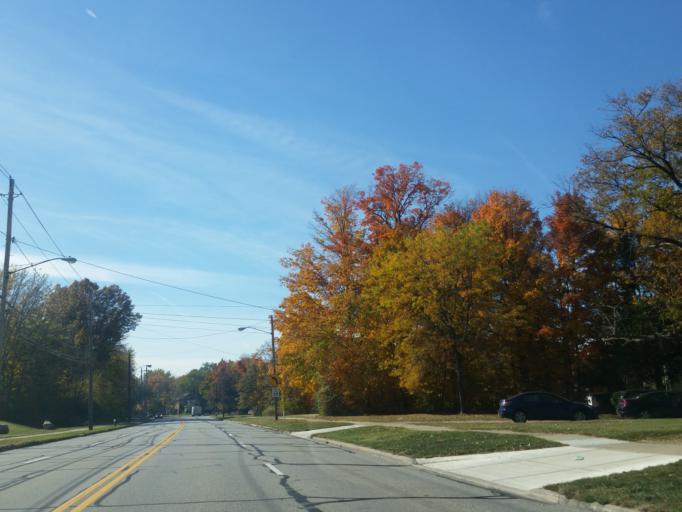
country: US
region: Ohio
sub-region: Cuyahoga County
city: Westlake
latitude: 41.4478
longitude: -81.9263
